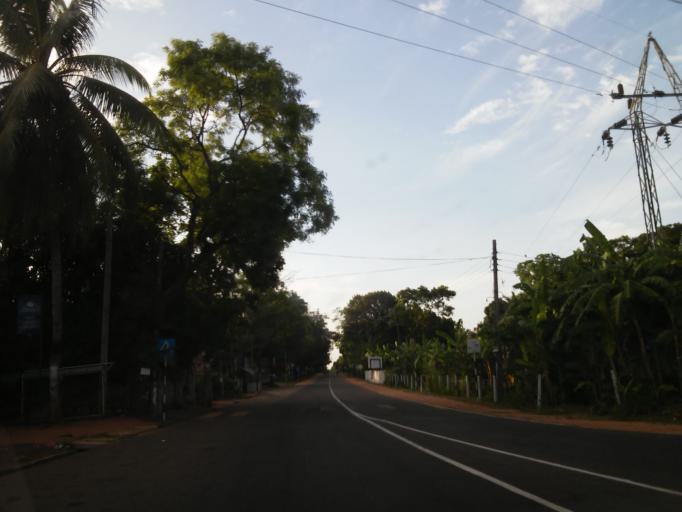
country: LK
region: North Central
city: Anuradhapura
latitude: 8.1275
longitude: 80.5626
